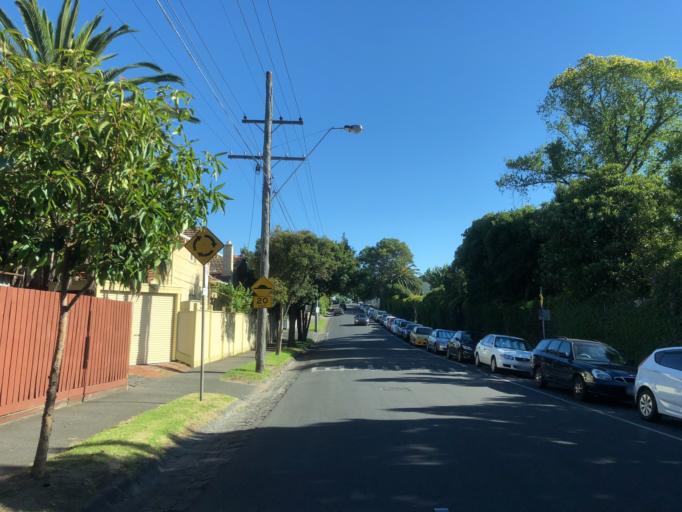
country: AU
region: Victoria
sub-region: Moonee Valley
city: Moonee Ponds
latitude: -37.7655
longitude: 144.9275
